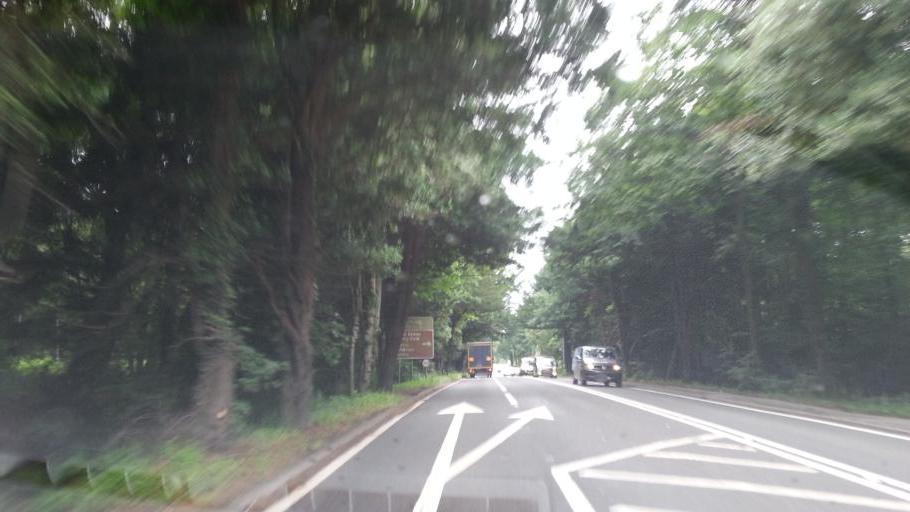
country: GB
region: England
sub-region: Nottinghamshire
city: Edwinstowe
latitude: 53.1749
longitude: -1.0430
